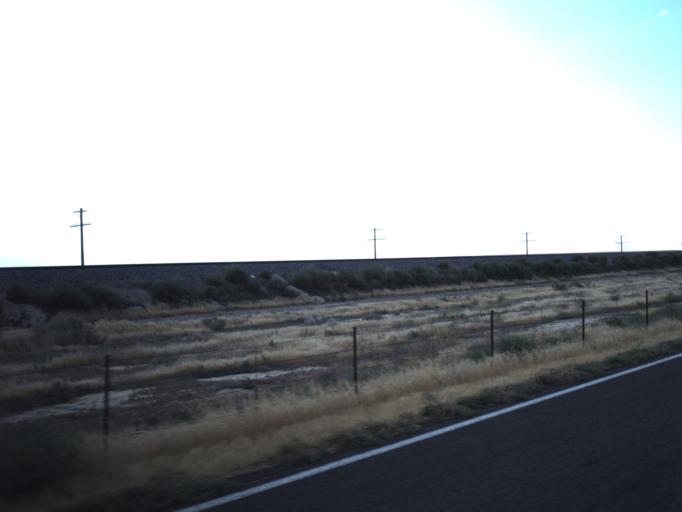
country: US
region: Utah
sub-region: Millard County
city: Delta
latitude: 38.9980
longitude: -112.7884
